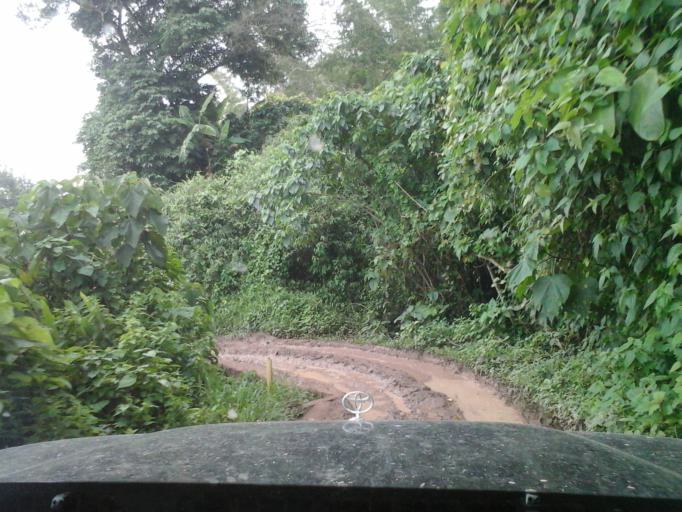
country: CO
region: Cesar
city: Agustin Codazzi
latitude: 9.9631
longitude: -73.0604
